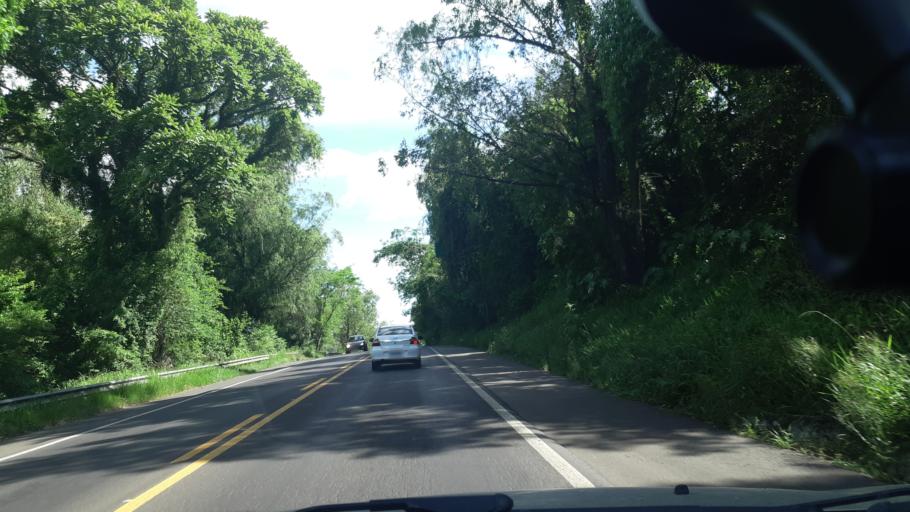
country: BR
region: Rio Grande do Sul
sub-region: Estancia Velha
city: Estancia Velha
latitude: -29.6418
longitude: -51.1427
